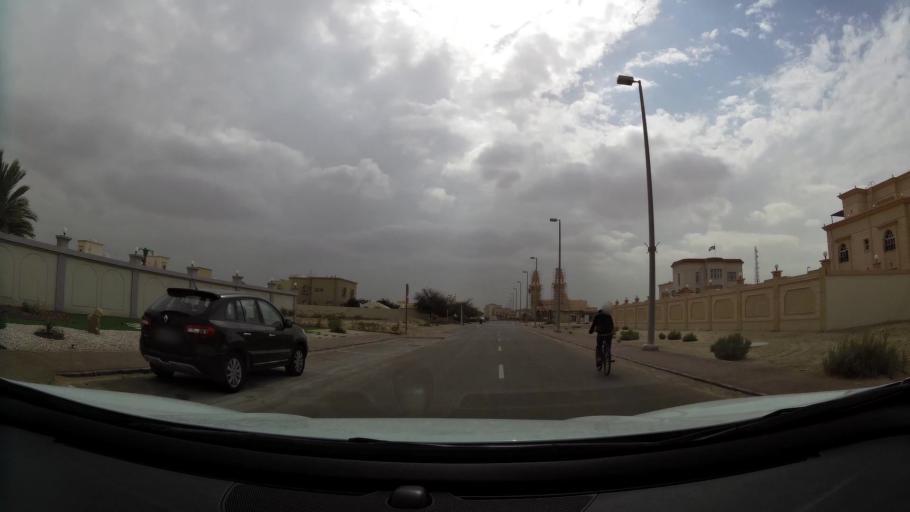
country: AE
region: Abu Dhabi
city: Abu Dhabi
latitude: 24.3852
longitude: 54.6425
